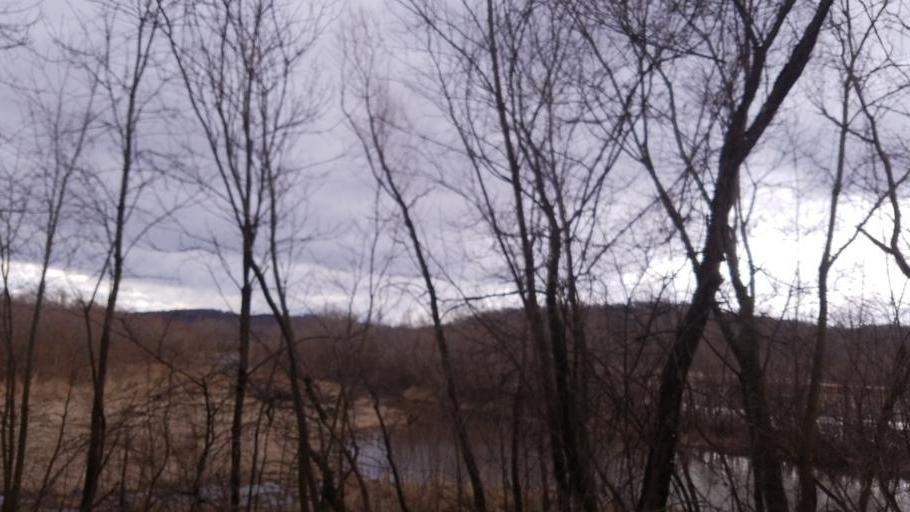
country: US
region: Ohio
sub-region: Muskingum County
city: Frazeysburg
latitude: 40.0277
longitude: -82.1217
